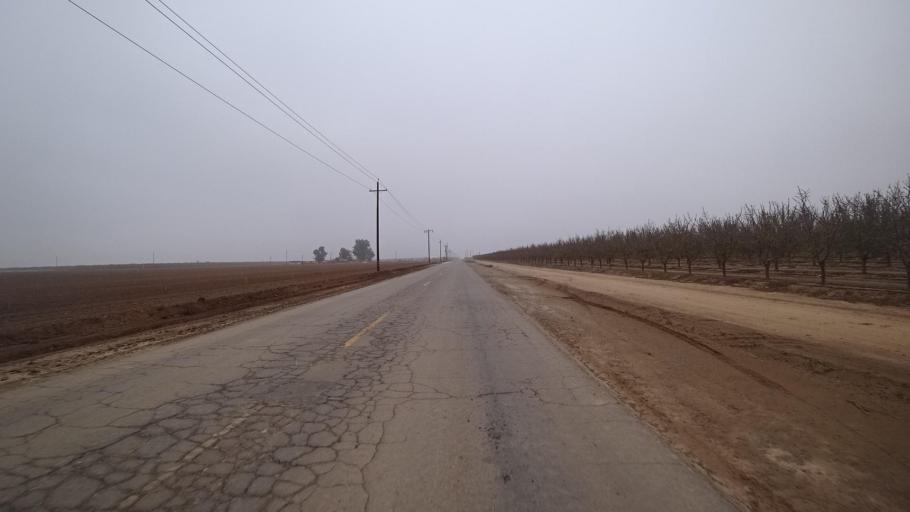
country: US
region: California
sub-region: Kern County
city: Wasco
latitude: 35.6122
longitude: -119.5091
